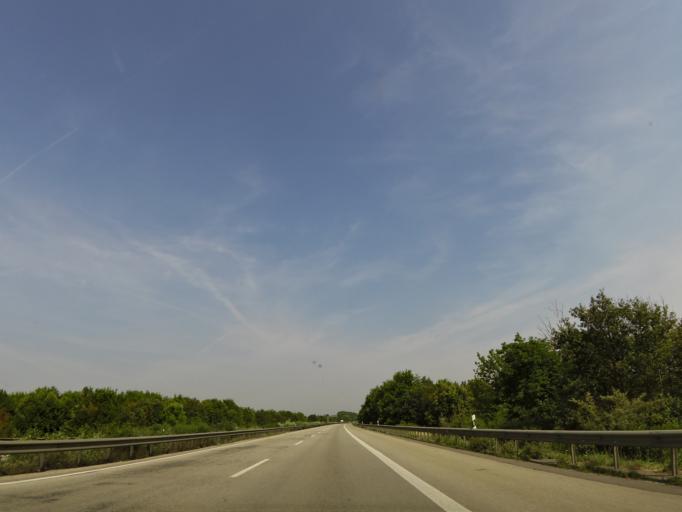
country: DE
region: Rheinland-Pfalz
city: Sprendlingen
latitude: 49.8458
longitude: 7.9853
